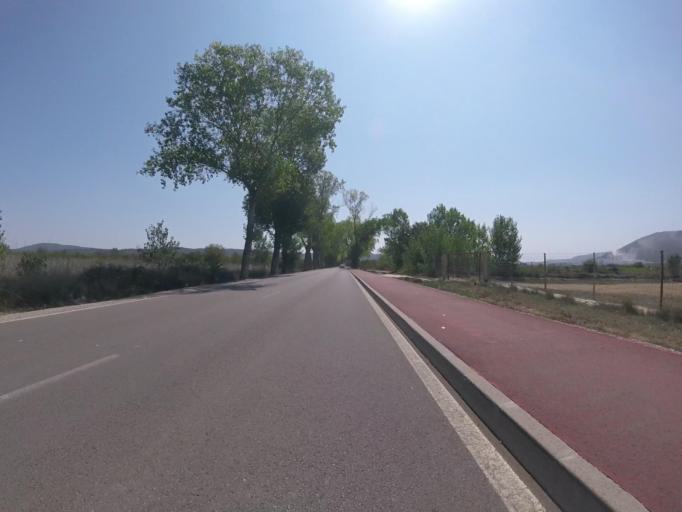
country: ES
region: Valencia
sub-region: Provincia de Castello
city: Cabanes
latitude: 40.1637
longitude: 0.0201
